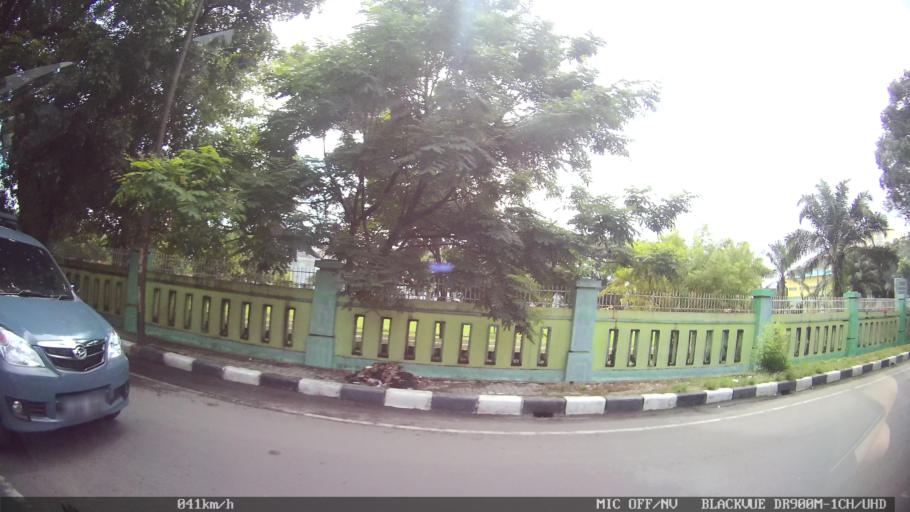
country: ID
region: North Sumatra
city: Medan
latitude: 3.6105
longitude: 98.7071
